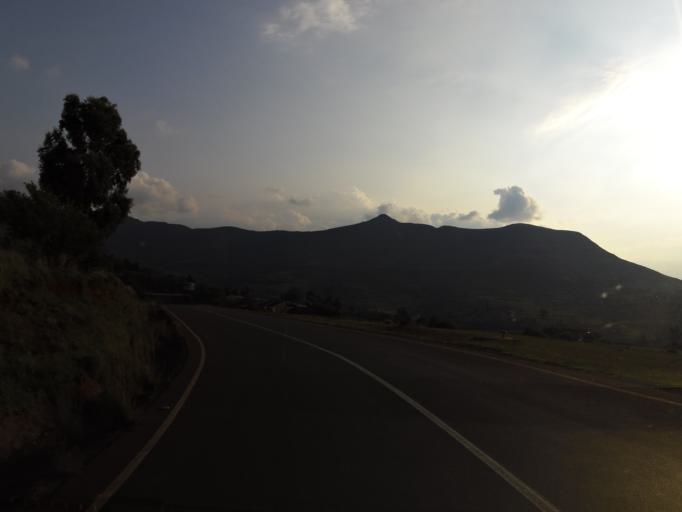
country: LS
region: Butha-Buthe
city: Butha-Buthe
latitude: -29.0327
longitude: 28.2853
